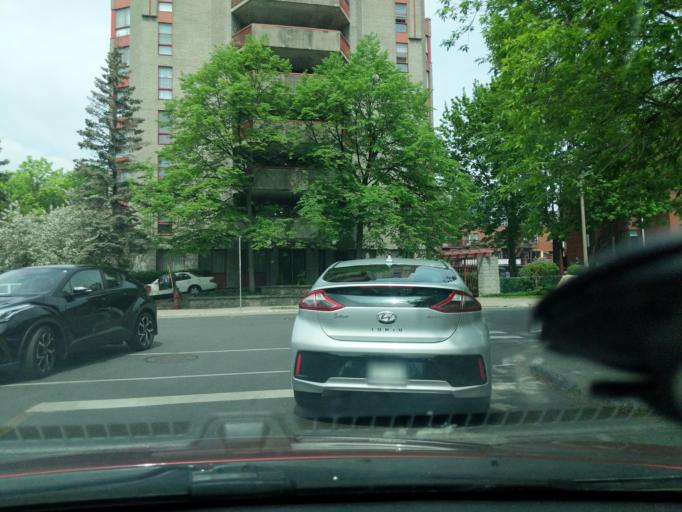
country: CA
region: Quebec
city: Westmount
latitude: 45.4838
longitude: -73.5774
